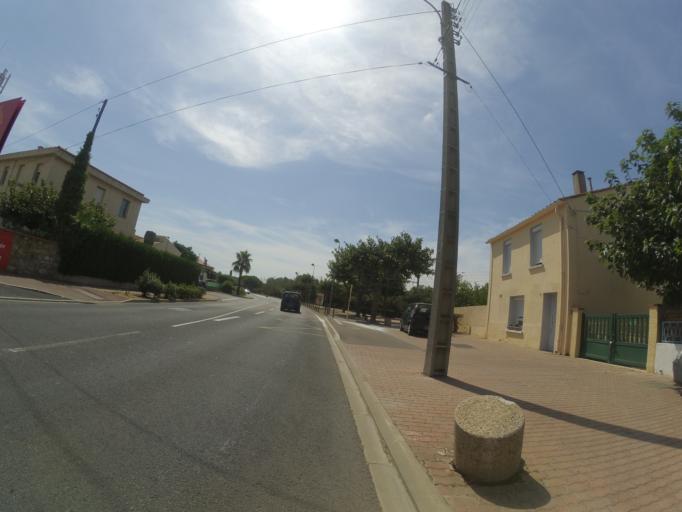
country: FR
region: Languedoc-Roussillon
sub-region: Departement des Pyrenees-Orientales
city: Rivesaltes
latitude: 42.7651
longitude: 2.8690
